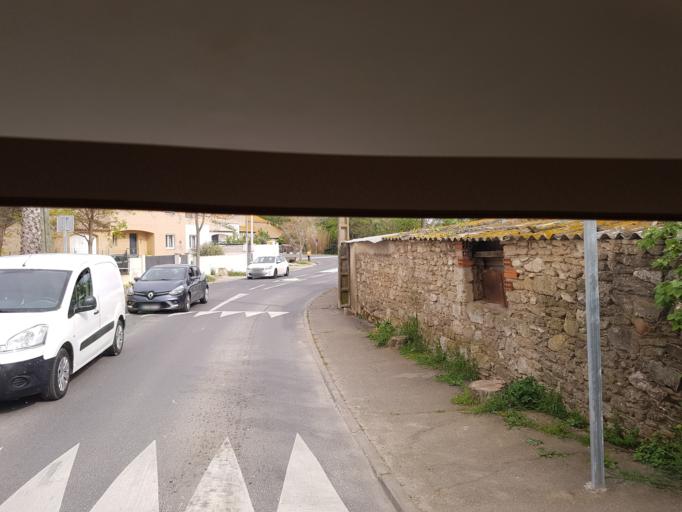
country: FR
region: Languedoc-Roussillon
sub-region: Departement de l'Herault
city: Vendres
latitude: 43.2692
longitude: 3.2208
